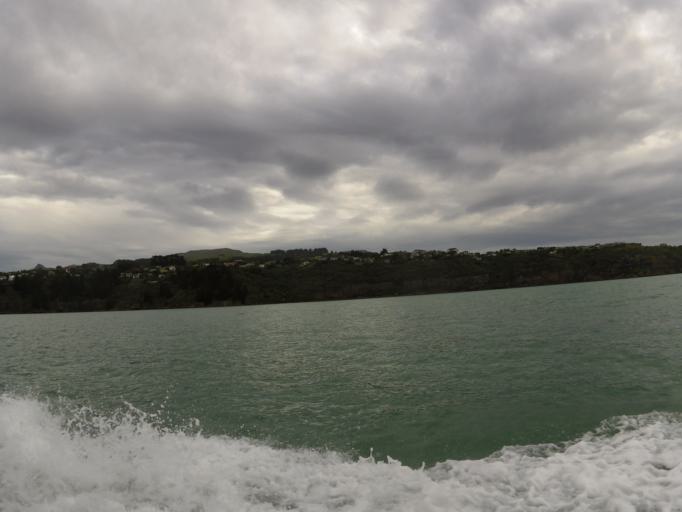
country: NZ
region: Canterbury
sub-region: Christchurch City
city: Christchurch
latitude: -43.6199
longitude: 172.7302
